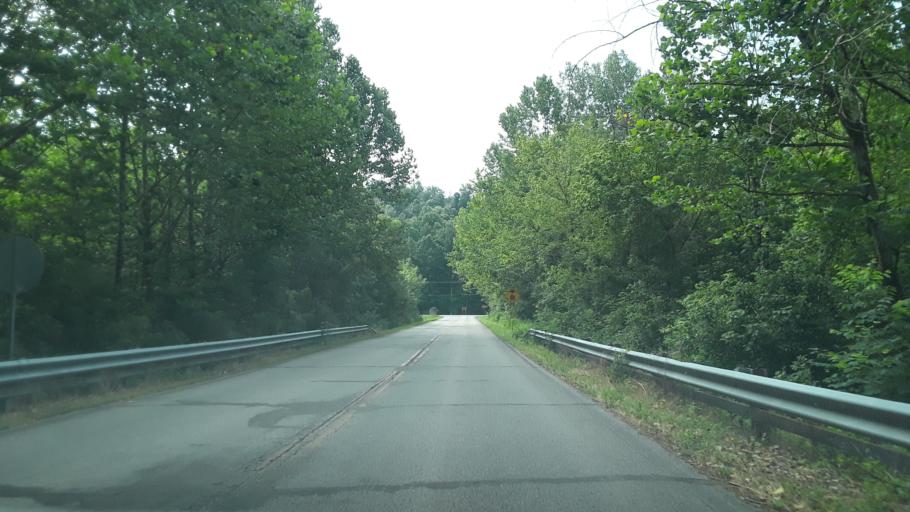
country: US
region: Indiana
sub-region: Clark County
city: Sellersburg
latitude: 38.4467
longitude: -85.8651
